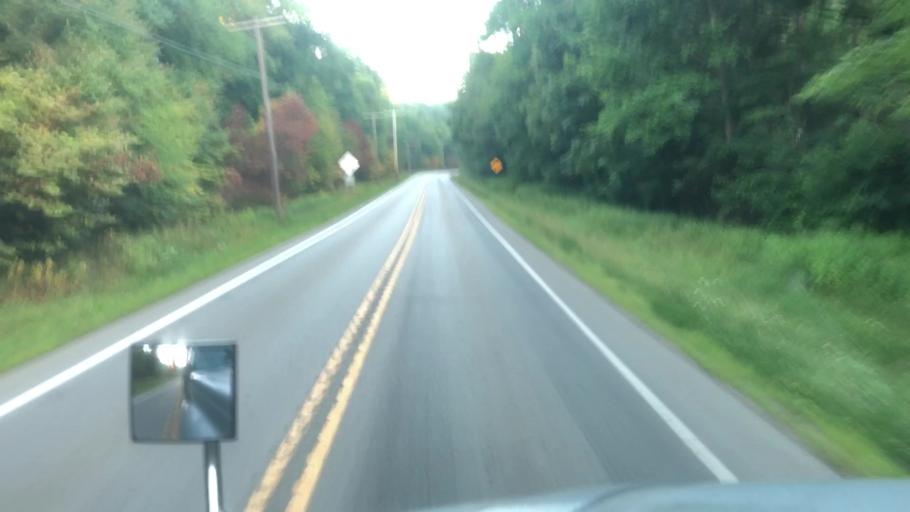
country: US
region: Pennsylvania
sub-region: Venango County
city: Hasson Heights
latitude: 41.4807
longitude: -79.6610
